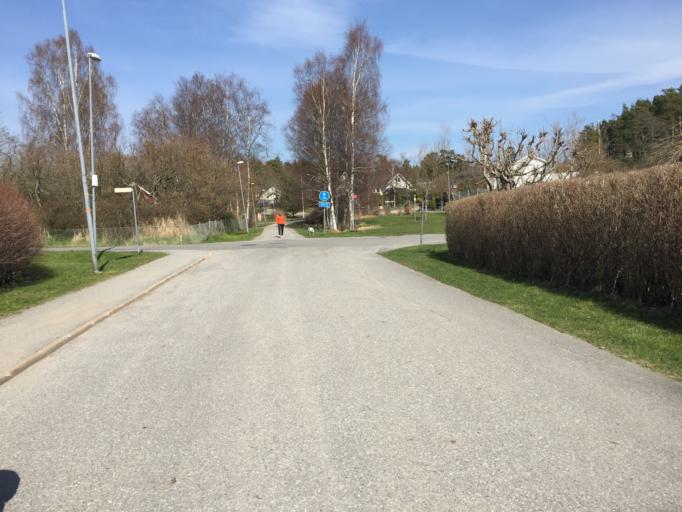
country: SE
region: Stockholm
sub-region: Nacka Kommun
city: Alta
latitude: 59.2727
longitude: 18.1747
